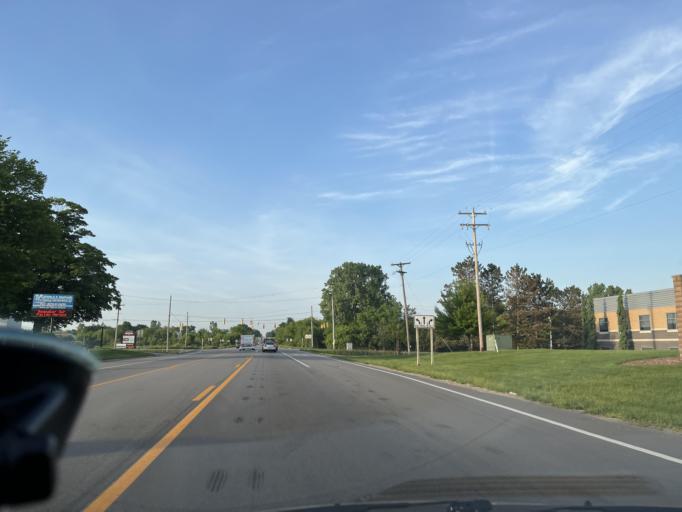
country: US
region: Michigan
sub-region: Kent County
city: Caledonia
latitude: 42.7842
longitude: -85.5068
